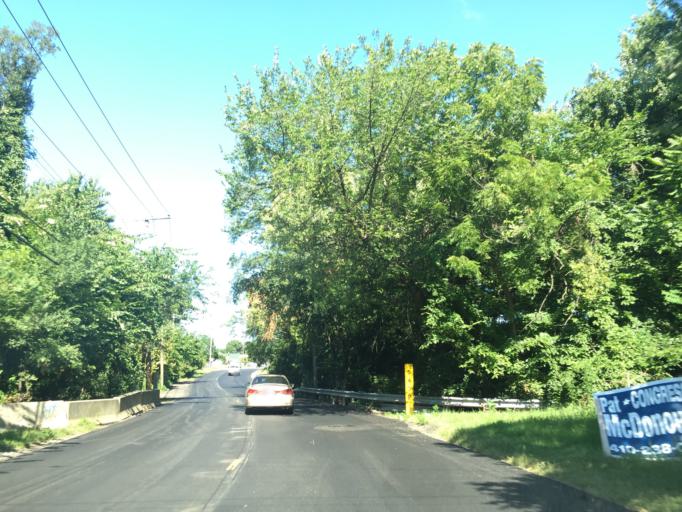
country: US
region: Maryland
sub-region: Baltimore County
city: Essex
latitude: 39.2824
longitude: -76.4941
